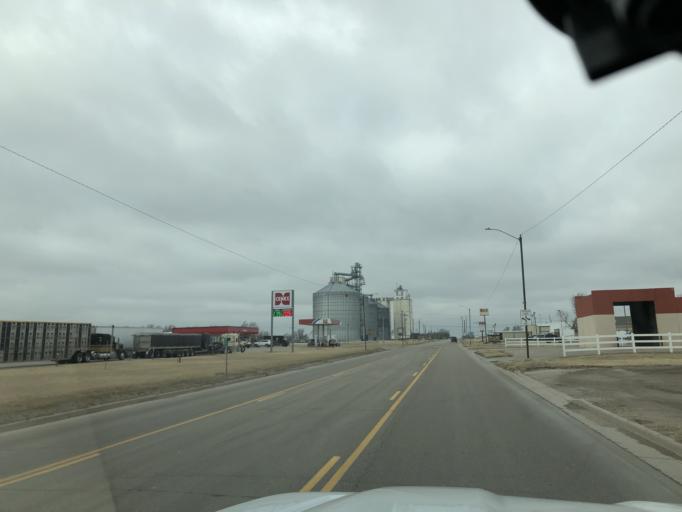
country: US
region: Kansas
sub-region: Stafford County
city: Stafford
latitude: 37.9548
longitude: -98.5938
